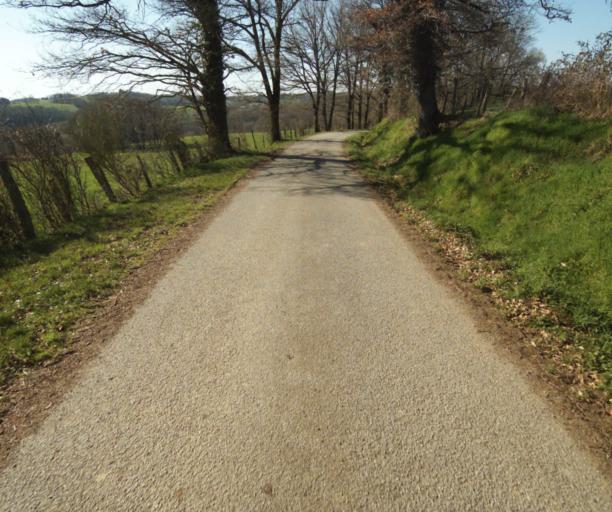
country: FR
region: Limousin
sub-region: Departement de la Correze
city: Chamboulive
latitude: 45.4810
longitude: 1.6878
